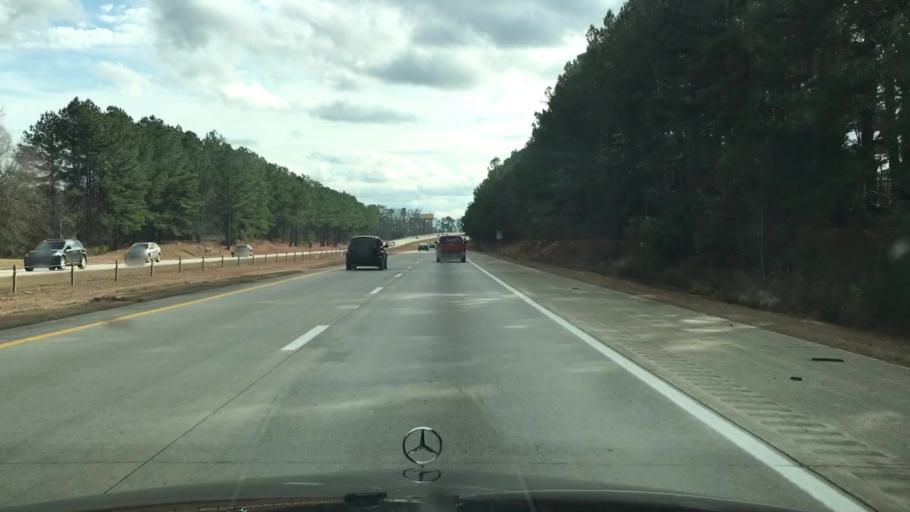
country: US
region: North Carolina
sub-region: Johnston County
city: Benson
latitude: 35.4162
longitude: -78.5269
